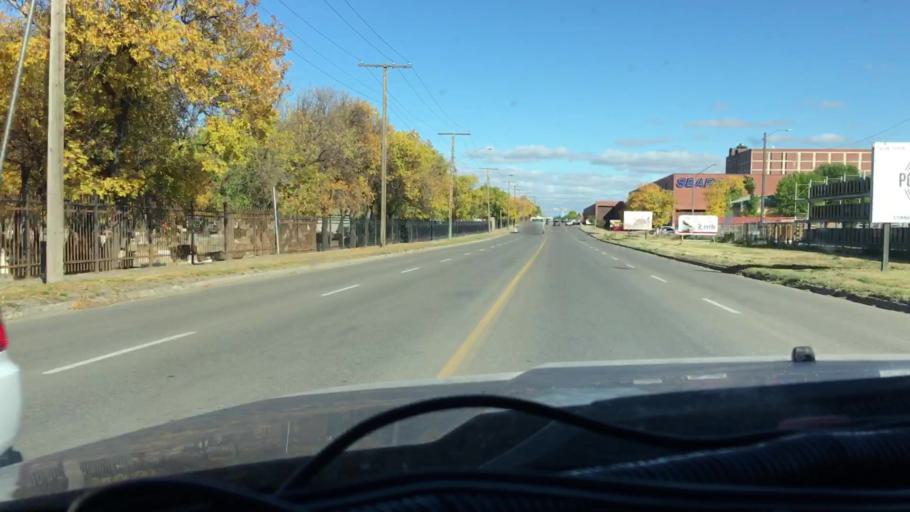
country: CA
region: Saskatchewan
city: Regina
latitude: 50.4629
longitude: -104.6132
